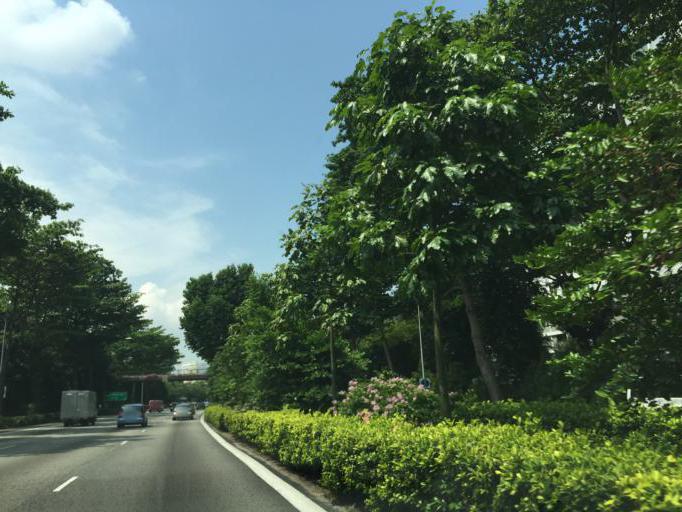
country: SG
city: Singapore
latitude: 1.3354
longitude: 103.9270
